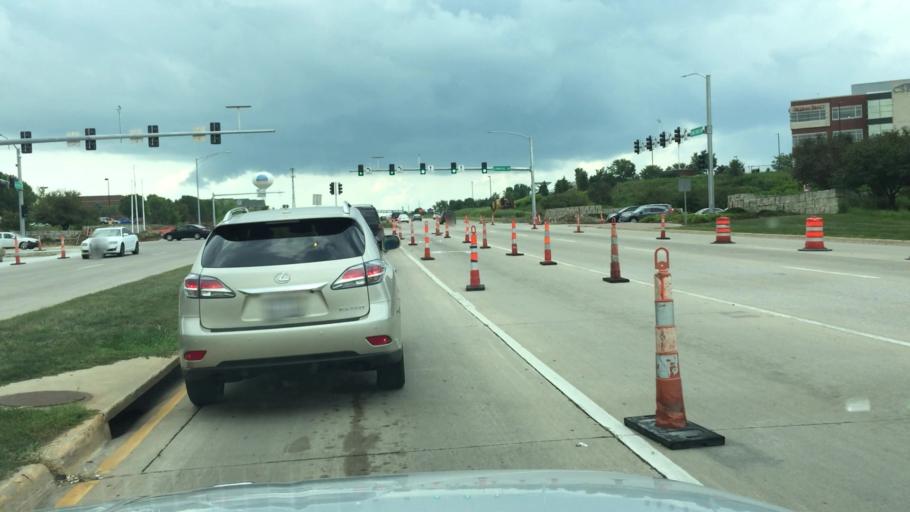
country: US
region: Iowa
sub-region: Johnson County
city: Coralville
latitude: 41.6952
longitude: -91.6085
